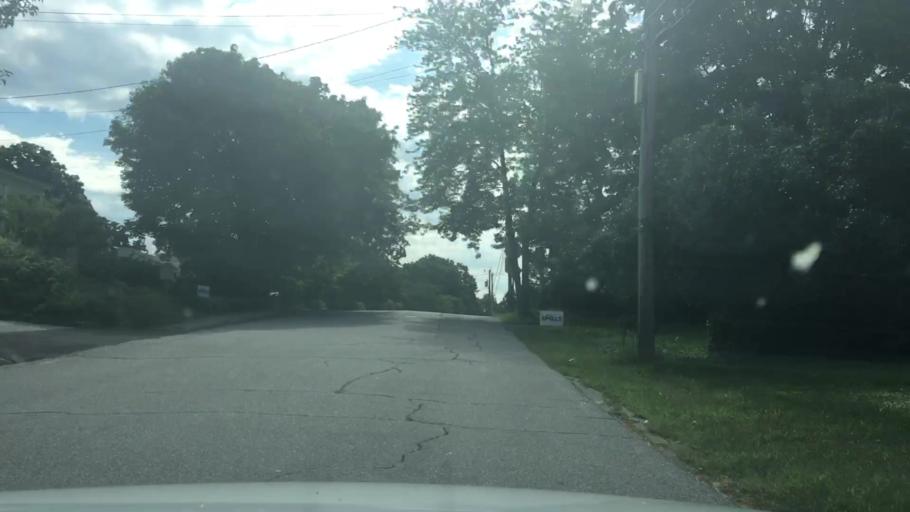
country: US
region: Maine
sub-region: Androscoggin County
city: Lewiston
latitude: 44.1110
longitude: -70.2035
